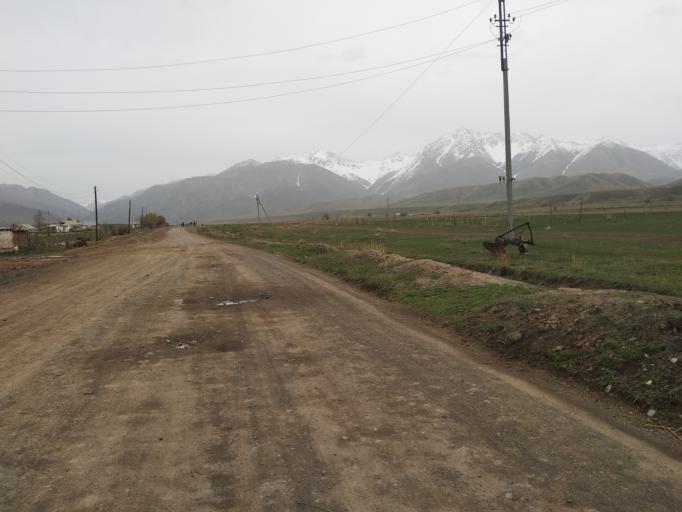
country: KG
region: Naryn
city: Naryn
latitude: 41.5189
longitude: 76.4410
